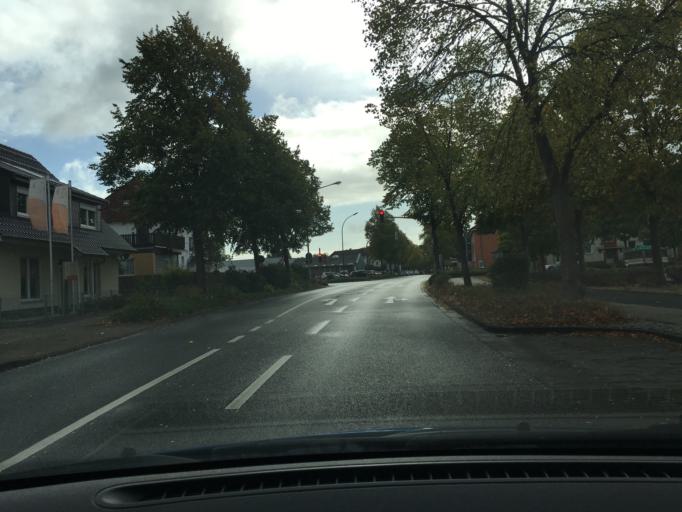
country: DE
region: Lower Saxony
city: Uelzen
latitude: 52.9679
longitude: 10.5738
